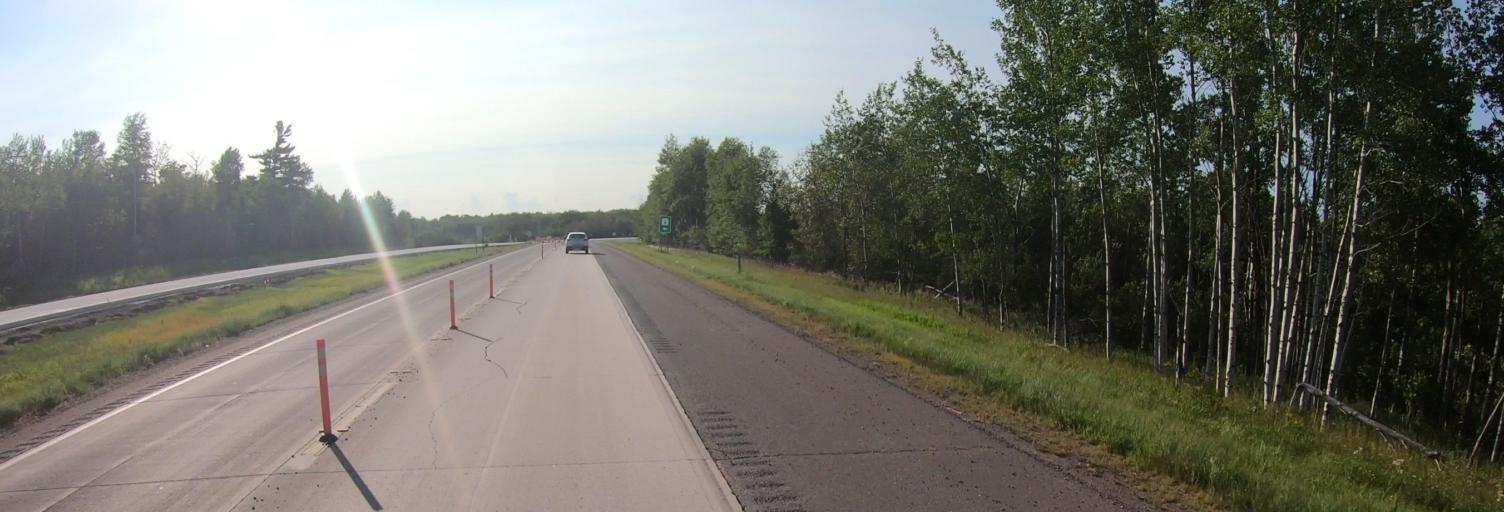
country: US
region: Minnesota
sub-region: Saint Louis County
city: Hermantown
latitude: 46.9228
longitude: -92.4084
